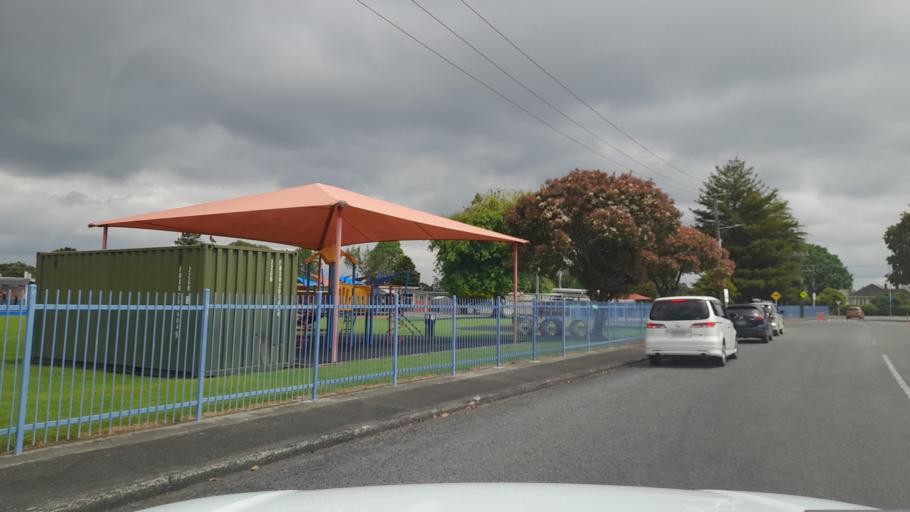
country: NZ
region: Northland
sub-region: Far North District
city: Waimate North
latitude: -35.4085
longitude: 173.8064
